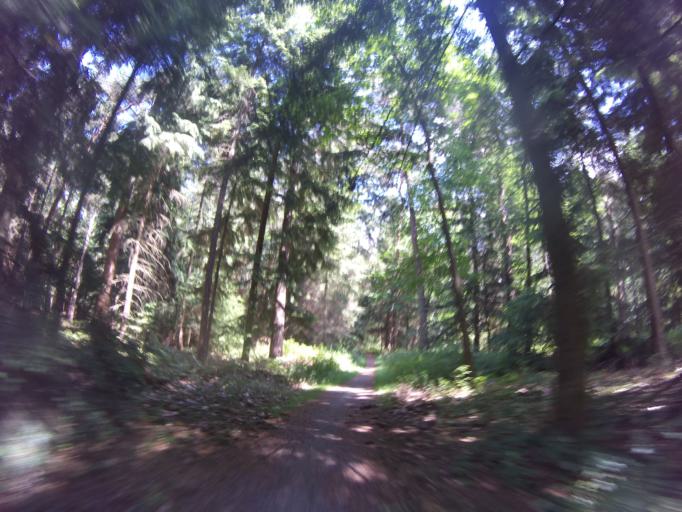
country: NL
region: Drenthe
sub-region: Gemeente Emmen
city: Emmen
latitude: 52.7938
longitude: 6.9112
